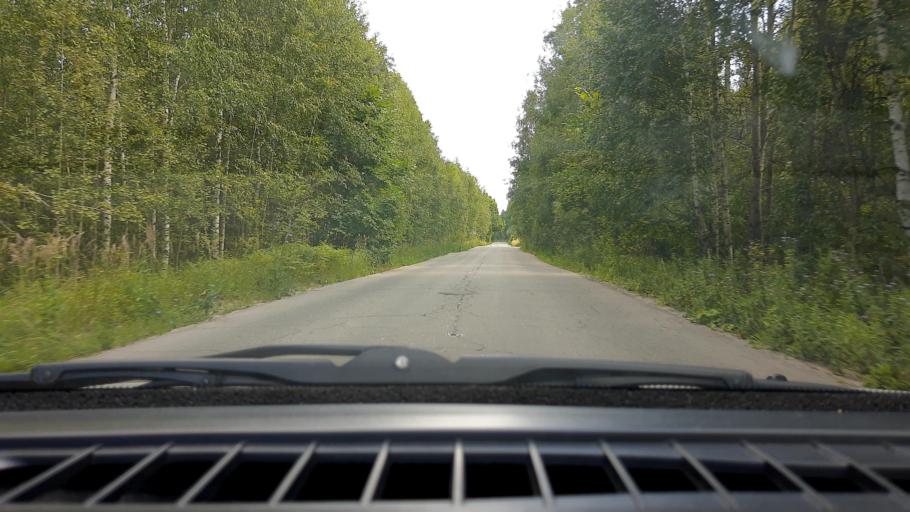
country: RU
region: Nizjnij Novgorod
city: Babino
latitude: 56.3155
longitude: 43.6241
